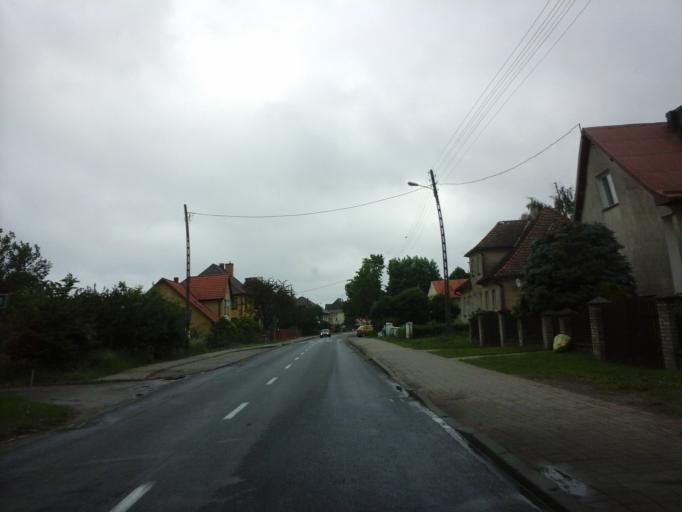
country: PL
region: West Pomeranian Voivodeship
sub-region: Powiat choszczenski
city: Drawno
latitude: 53.2161
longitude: 15.7512
